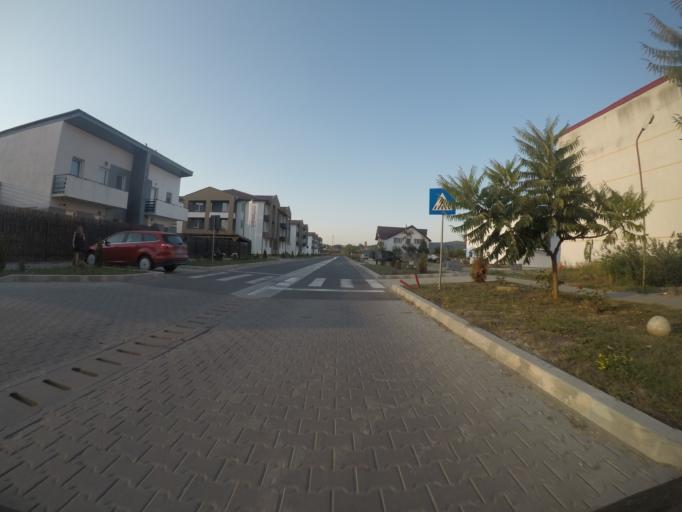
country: RO
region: Sibiu
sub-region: Comuna Selimbar
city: Selimbar
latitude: 45.7828
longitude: 24.1820
